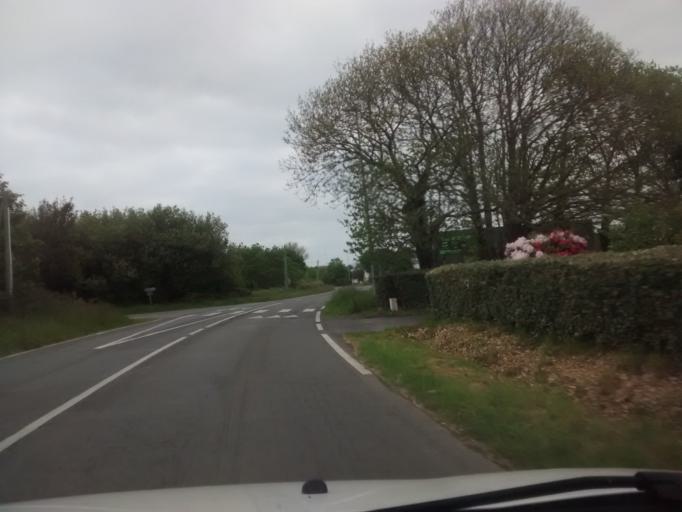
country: FR
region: Brittany
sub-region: Departement des Cotes-d'Armor
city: Tregastel
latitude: 48.8022
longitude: -3.4739
